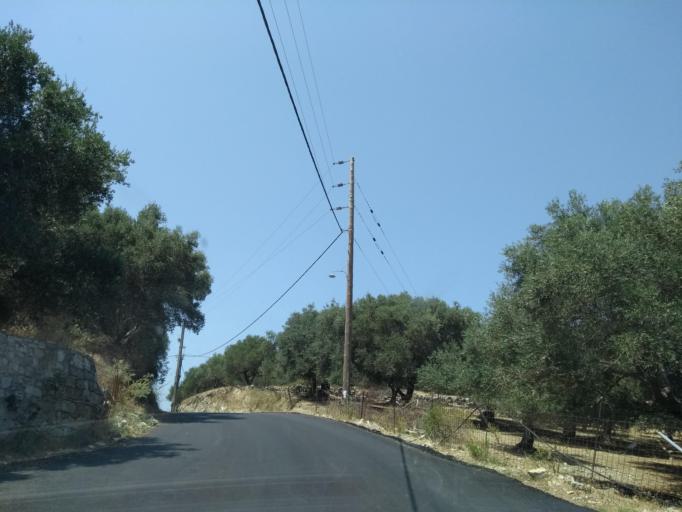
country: GR
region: Crete
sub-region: Nomos Chanias
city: Georgioupolis
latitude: 35.3205
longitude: 24.3004
